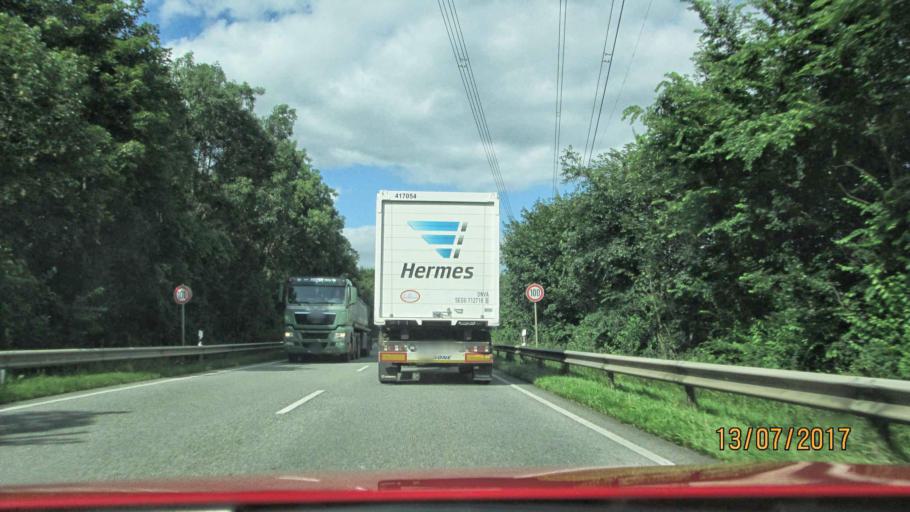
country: DE
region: Lower Saxony
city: Handorf
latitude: 53.3495
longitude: 10.3378
